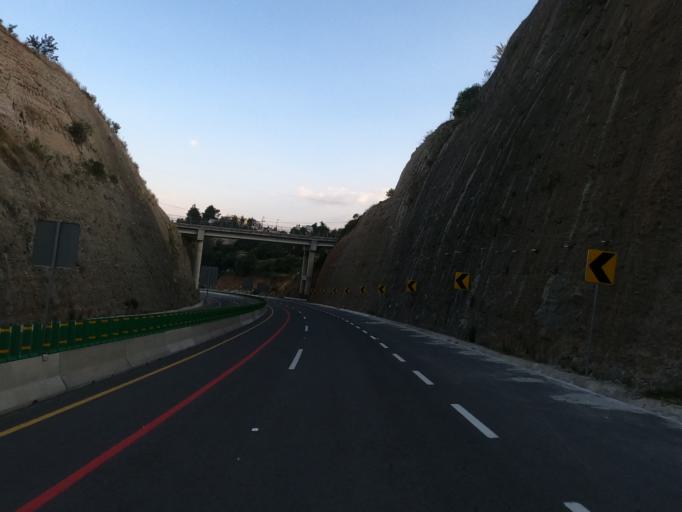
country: MX
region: Mexico
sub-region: Naucalpan de Juarez
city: Llano de las Flores (Barrio del Hueso)
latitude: 19.4248
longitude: -99.3320
